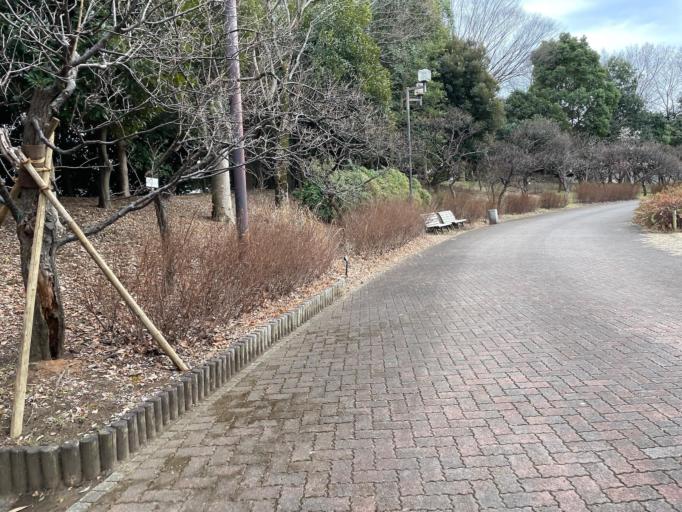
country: JP
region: Tokyo
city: Kokubunji
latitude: 35.6540
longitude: 139.4747
